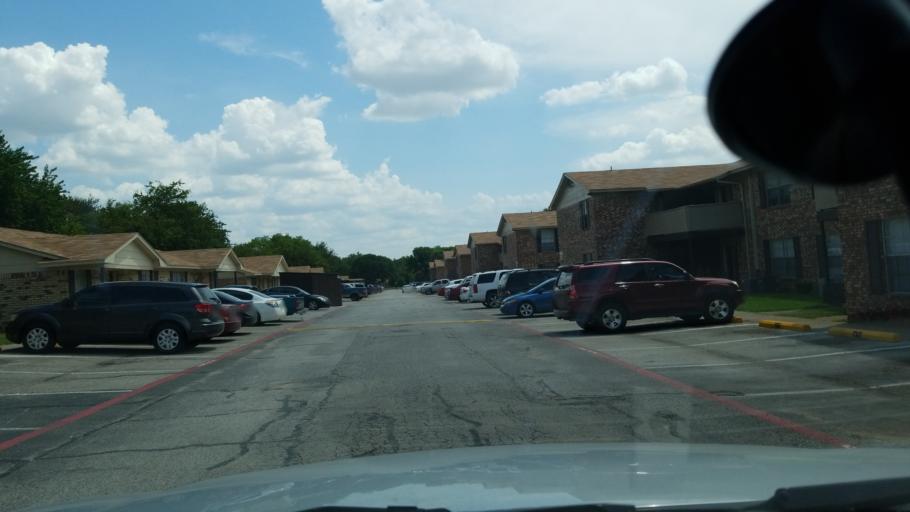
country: US
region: Texas
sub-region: Dallas County
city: Irving
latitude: 32.8284
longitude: -96.9819
